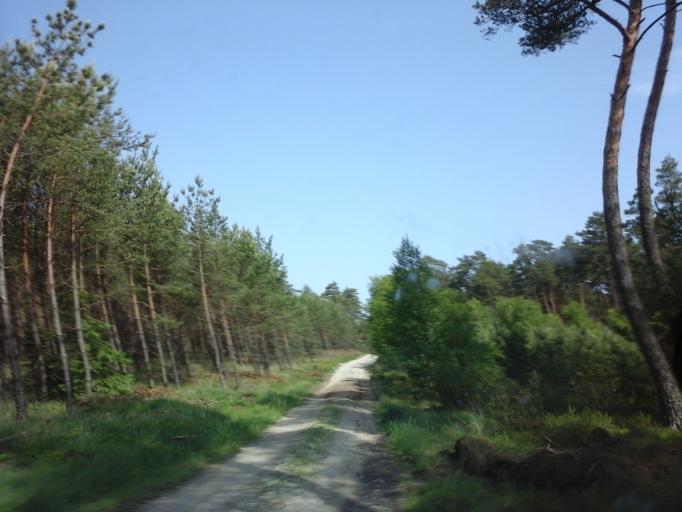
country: PL
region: West Pomeranian Voivodeship
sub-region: Powiat choszczenski
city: Drawno
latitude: 53.1639
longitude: 15.7535
